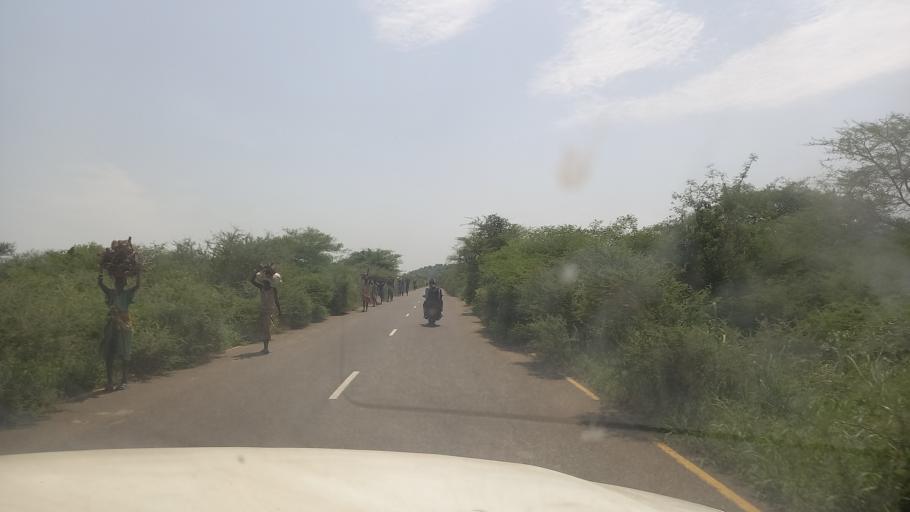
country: ET
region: Gambela
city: Gambela
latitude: 8.2800
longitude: 34.2258
